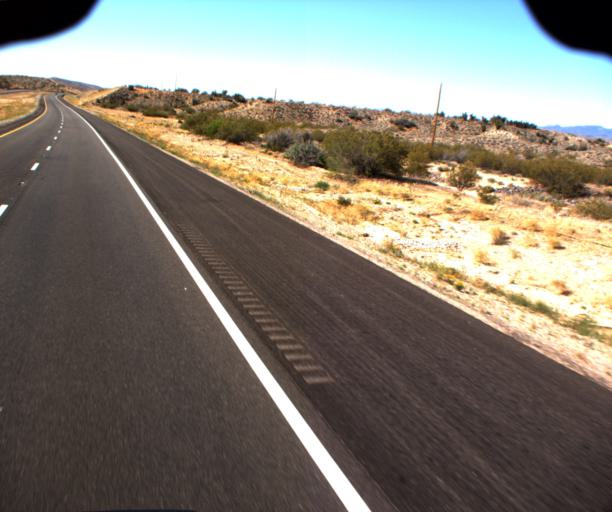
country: US
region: Arizona
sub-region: Mohave County
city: Kingman
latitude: 35.0196
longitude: -113.6647
